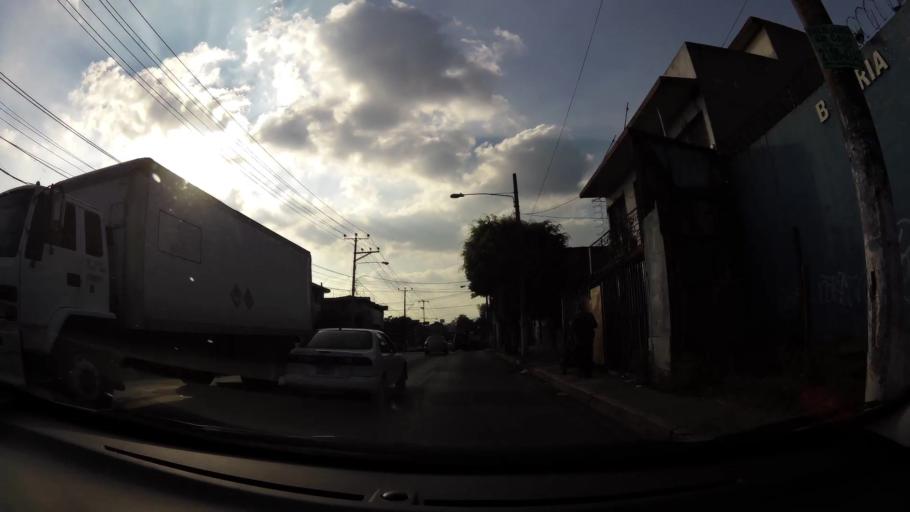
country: SV
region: San Salvador
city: San Salvador
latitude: 13.6922
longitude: -89.1979
